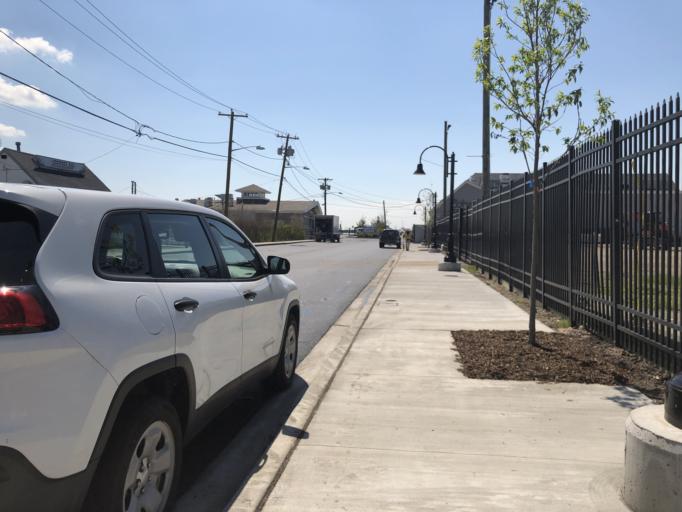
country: US
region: New York
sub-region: Suffolk County
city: Bay Shore
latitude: 40.7159
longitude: -73.2416
